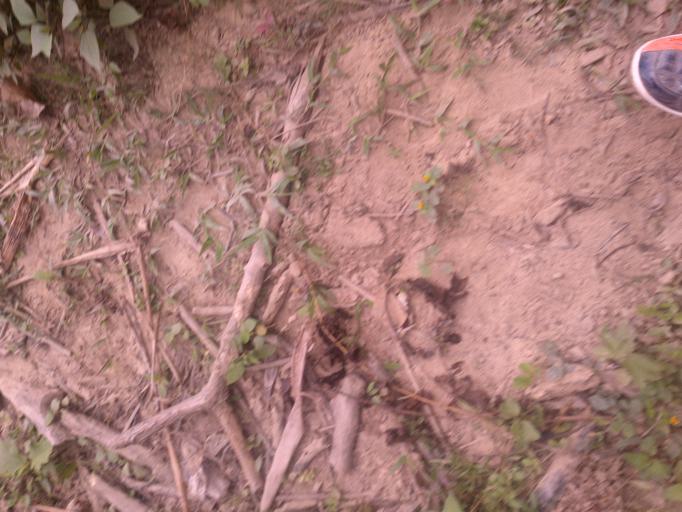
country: LA
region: Xiangkhoang
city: Muang Phonsavan
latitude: 19.3379
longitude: 103.6191
